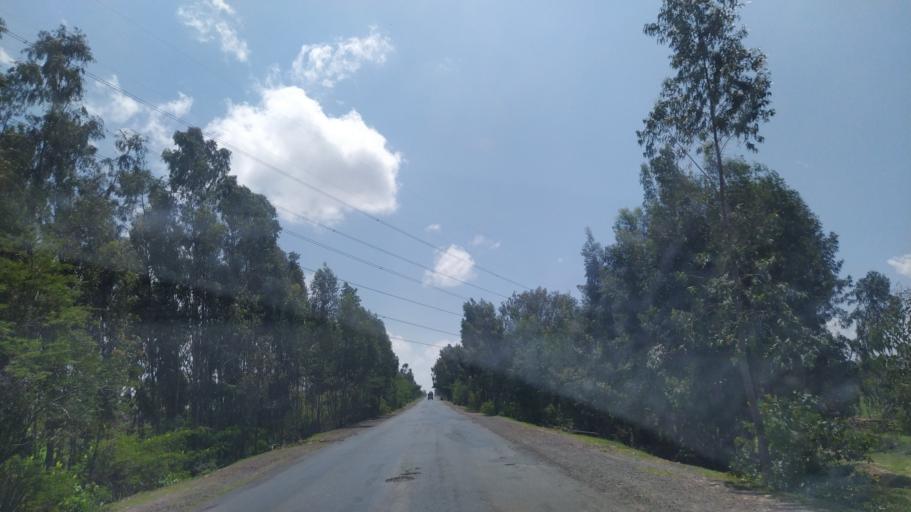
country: ET
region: Southern Nations, Nationalities, and People's Region
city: Butajira
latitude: 7.7543
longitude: 38.1299
